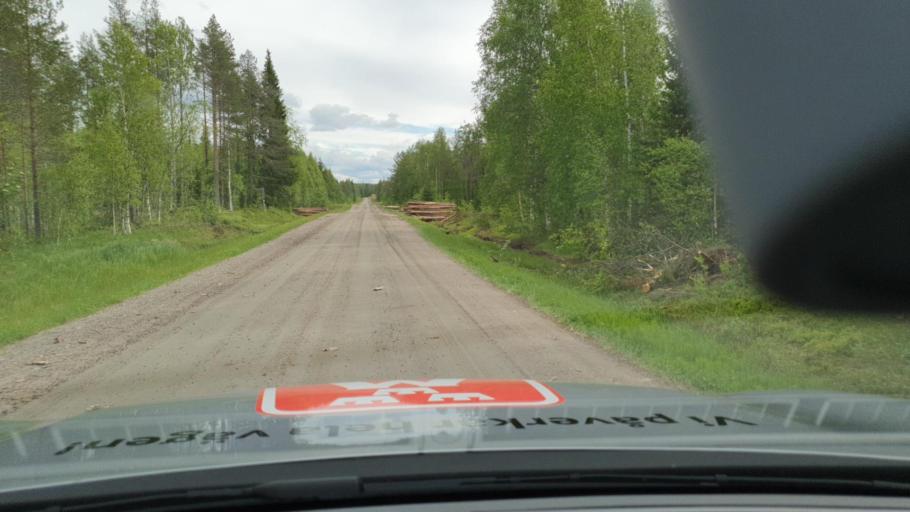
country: FI
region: Lapland
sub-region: Torniolaakso
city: Ylitornio
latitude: 65.9521
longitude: 23.5801
